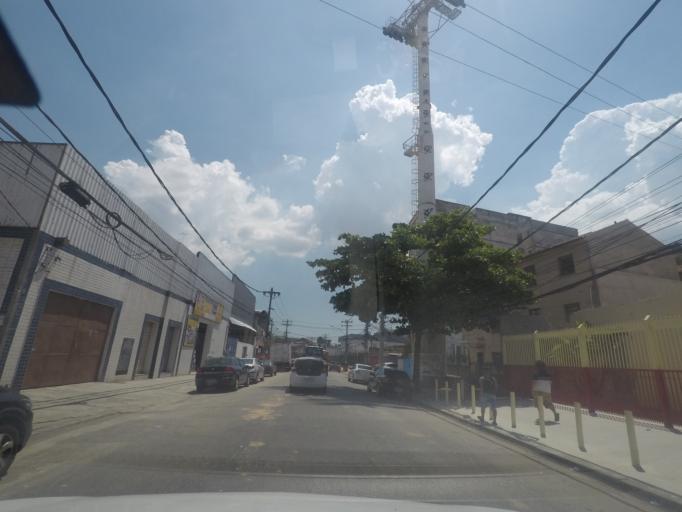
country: BR
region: Rio de Janeiro
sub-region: Rio De Janeiro
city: Rio de Janeiro
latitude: -22.8669
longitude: -43.2568
